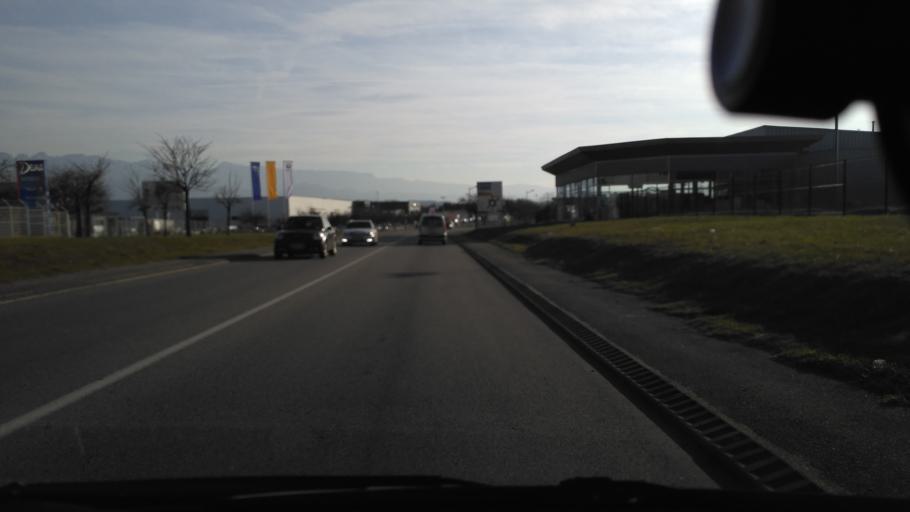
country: FR
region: Rhone-Alpes
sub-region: Departement de la Drome
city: Bourg-de-Peage
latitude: 45.0462
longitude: 5.0843
